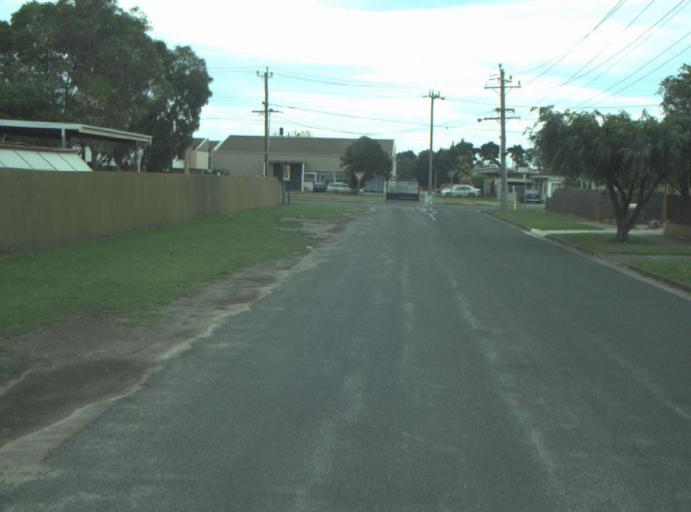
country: AU
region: Victoria
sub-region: Greater Geelong
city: Breakwater
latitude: -38.1786
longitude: 144.3708
